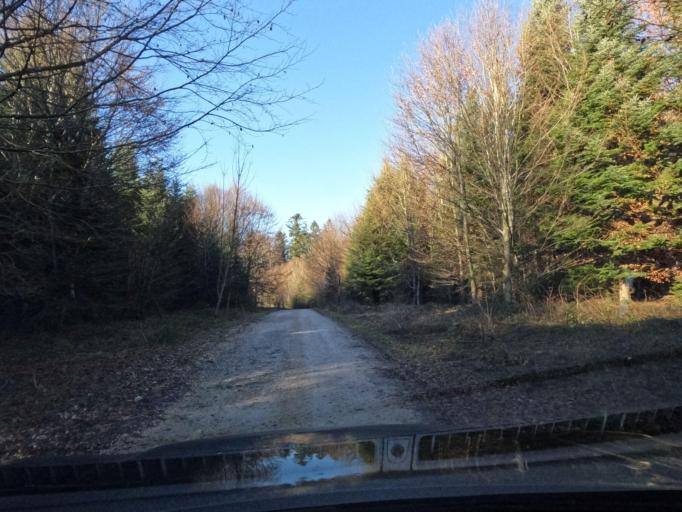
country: DE
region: Bavaria
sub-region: Upper Bavaria
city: Surberg
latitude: 47.8881
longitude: 12.6830
